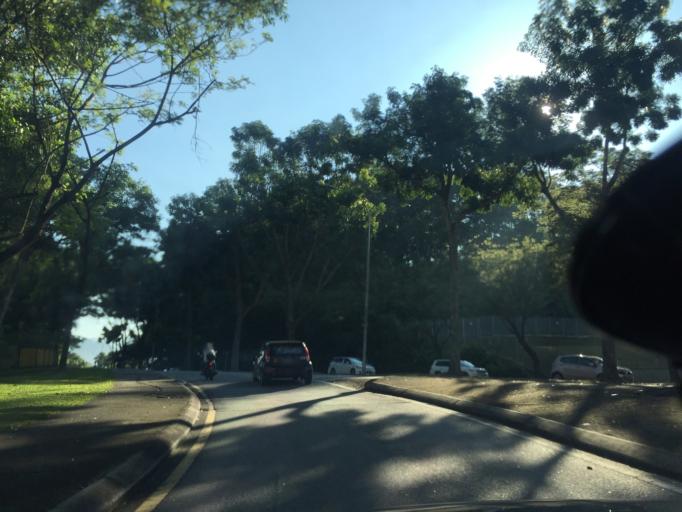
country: MY
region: Kuala Lumpur
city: Kuala Lumpur
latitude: 3.2045
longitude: 101.7375
